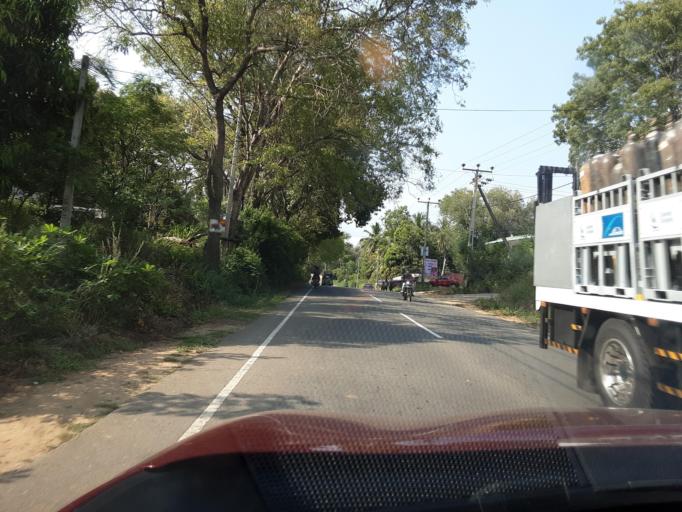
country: LK
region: Uva
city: Haputale
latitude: 6.5940
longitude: 81.1421
